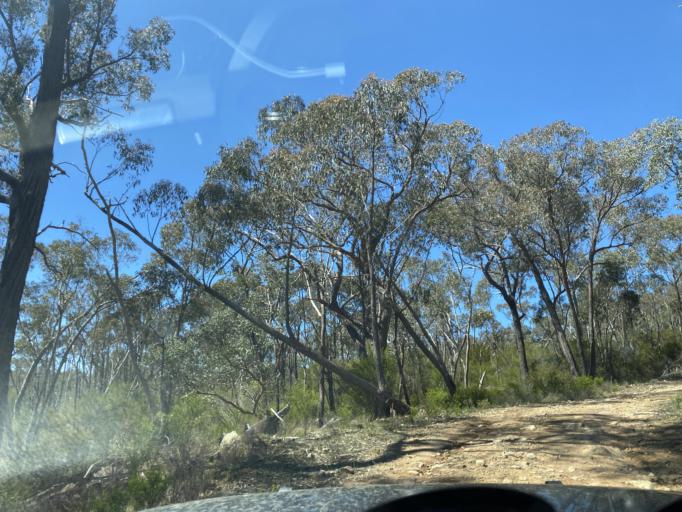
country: AU
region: Victoria
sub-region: Benalla
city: Benalla
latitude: -36.6975
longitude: 146.1514
